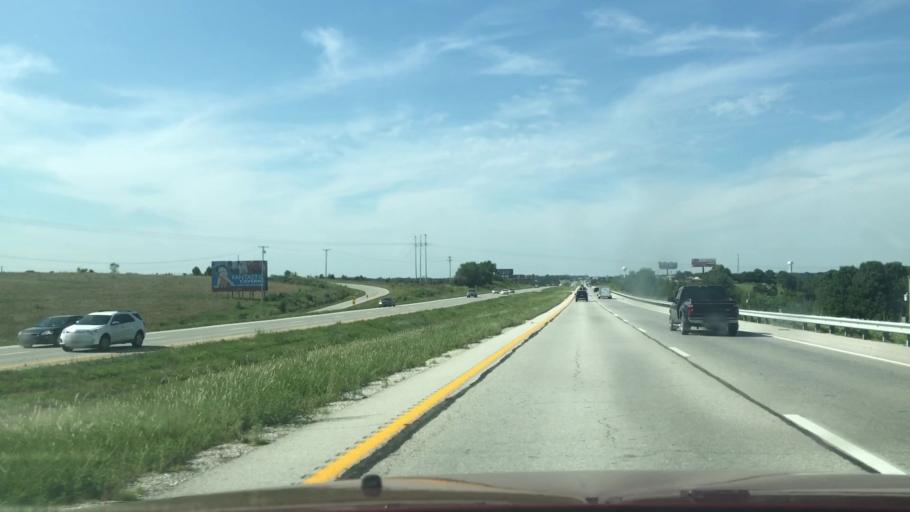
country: US
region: Missouri
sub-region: Christian County
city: Ozark
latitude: 36.9765
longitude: -93.2310
